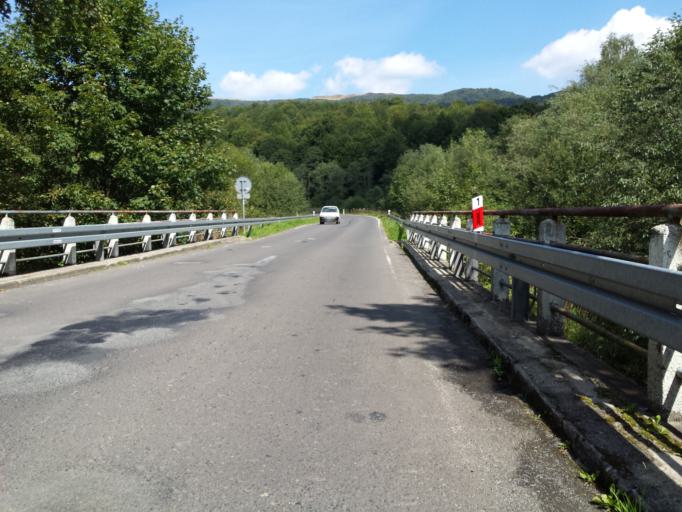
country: PL
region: Subcarpathian Voivodeship
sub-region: Powiat bieszczadzki
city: Lutowiska
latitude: 49.1060
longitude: 22.6286
